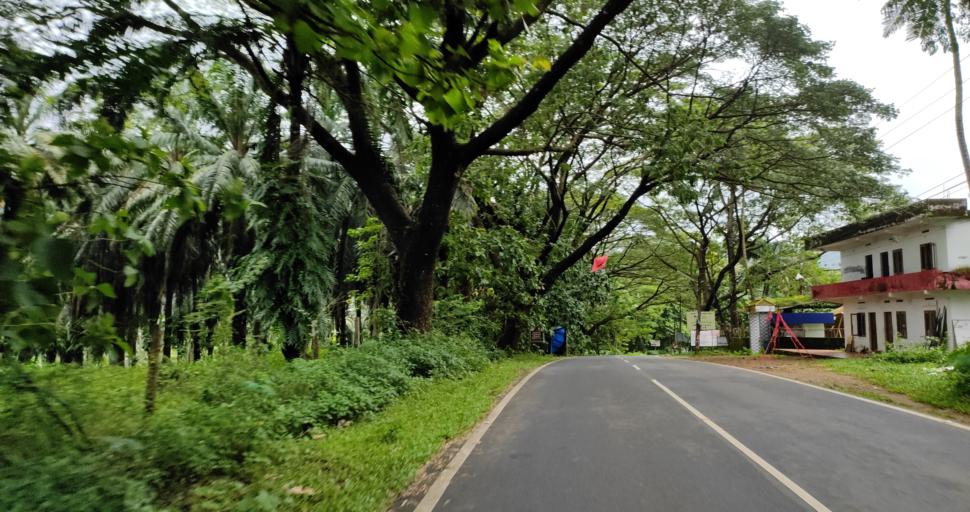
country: IN
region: Kerala
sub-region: Ernakulam
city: Angamali
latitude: 10.2952
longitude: 76.4842
